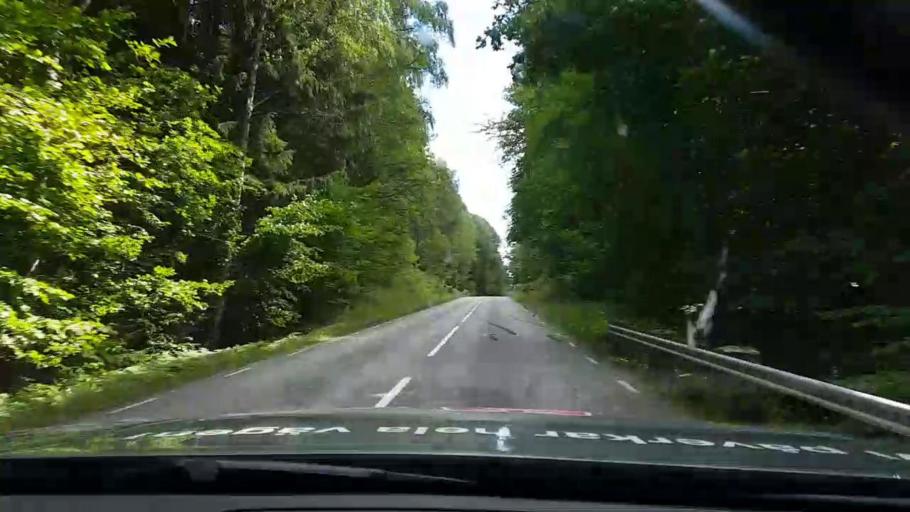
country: SE
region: Kalmar
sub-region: Vasterviks Kommun
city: Overum
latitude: 58.0663
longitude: 16.3959
